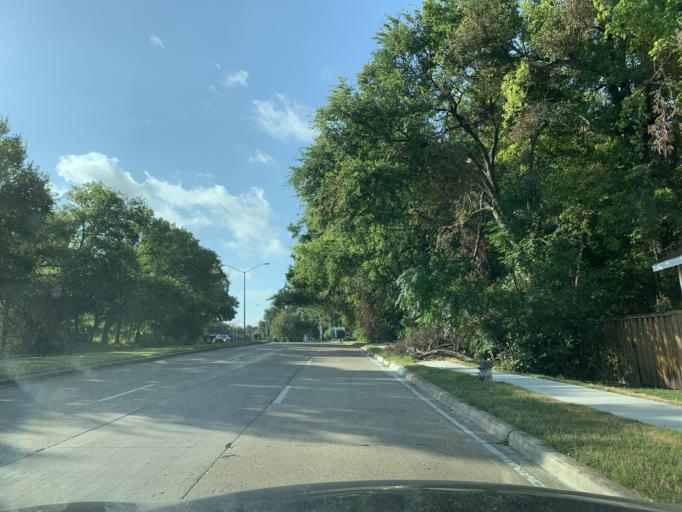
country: US
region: Texas
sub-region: Dallas County
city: Hutchins
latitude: 32.6805
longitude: -96.7664
